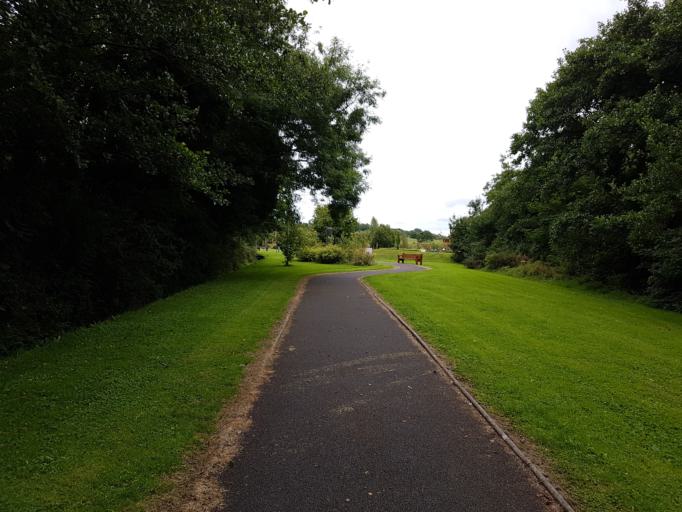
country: IE
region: Munster
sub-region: An Clar
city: Newmarket on Fergus
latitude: 52.7596
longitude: -8.8941
